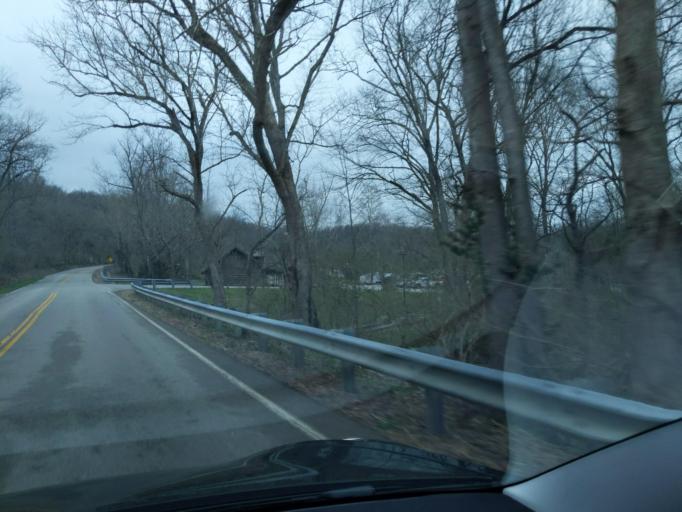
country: US
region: Kentucky
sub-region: Clark County
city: Winchester
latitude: 37.8973
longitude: -84.2679
